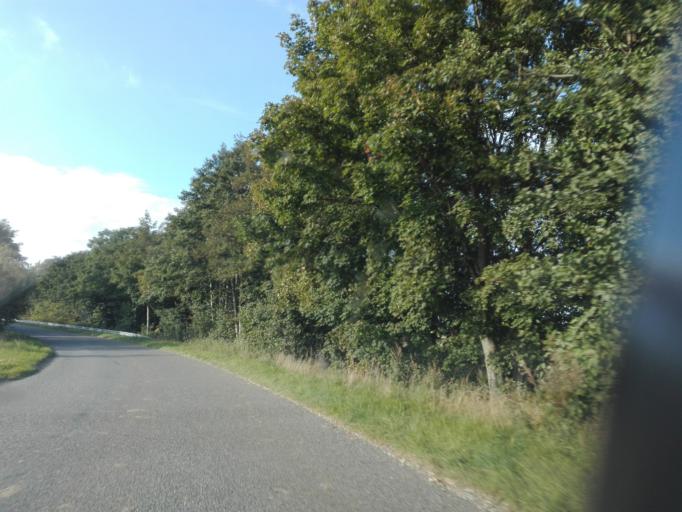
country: DK
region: Central Jutland
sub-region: Arhus Kommune
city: Malling
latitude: 56.0121
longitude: 10.1765
